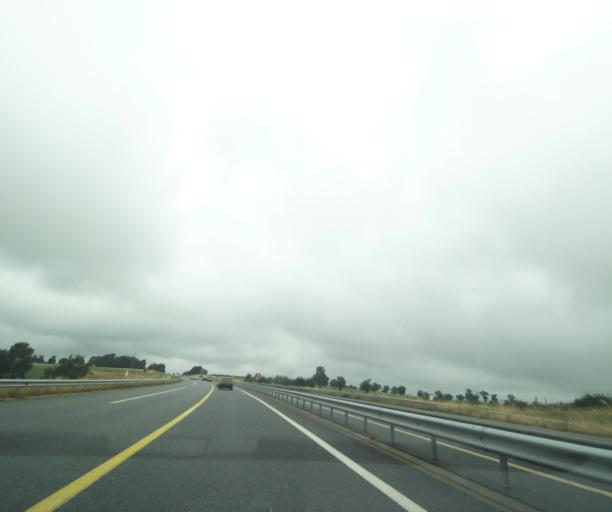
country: FR
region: Midi-Pyrenees
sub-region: Departement de l'Aveyron
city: Luc-la-Primaube
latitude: 44.2936
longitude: 2.5199
